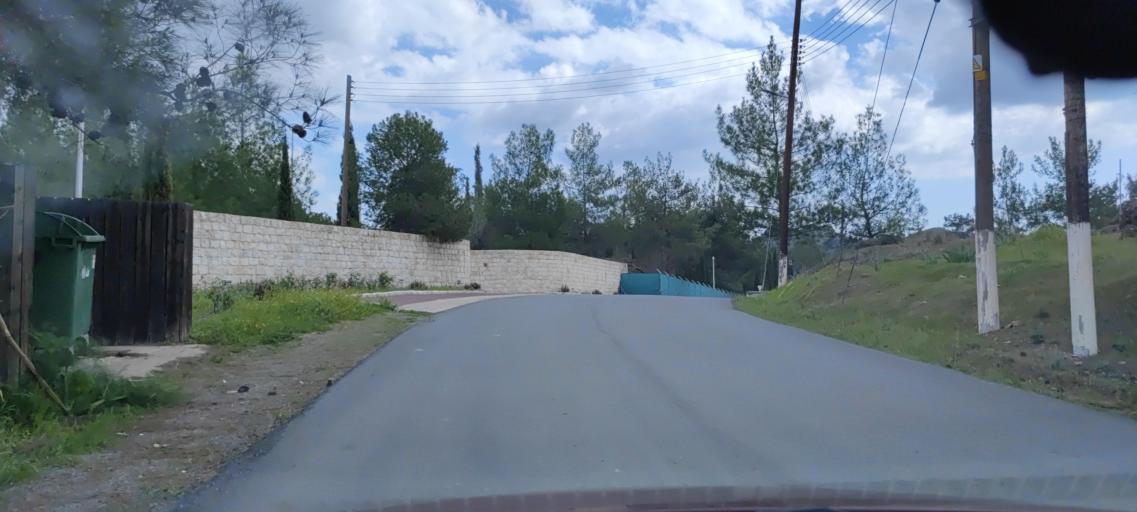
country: CY
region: Larnaka
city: Kornos
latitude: 34.9154
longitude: 33.3643
